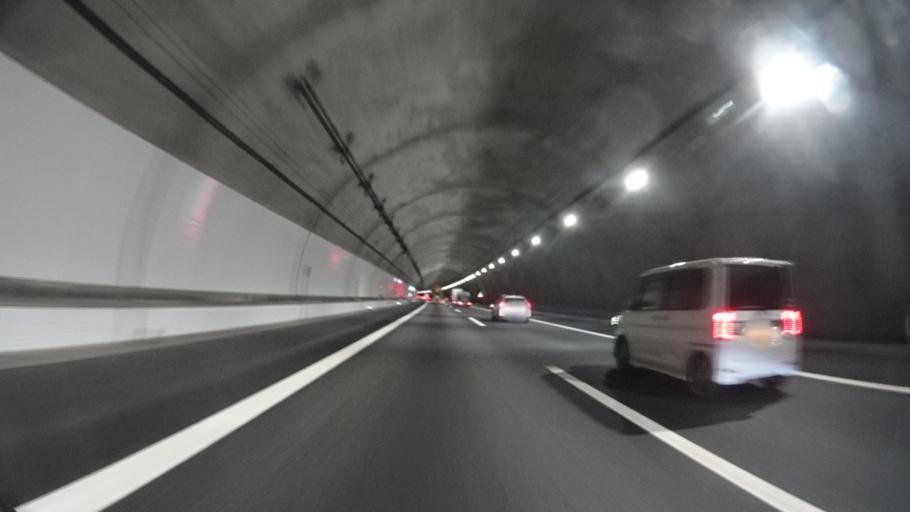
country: JP
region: Shiga Prefecture
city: Kusatsu
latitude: 34.9454
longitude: 136.0256
